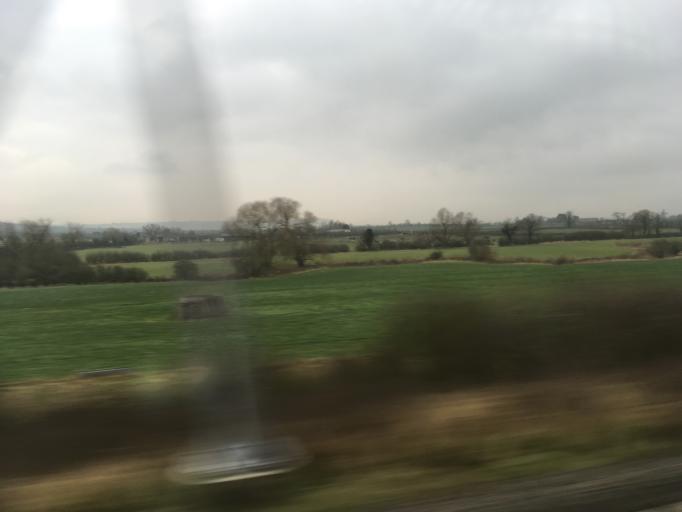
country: GB
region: England
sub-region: Wiltshire
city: Lyneham
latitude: 51.5563
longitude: -1.9636
